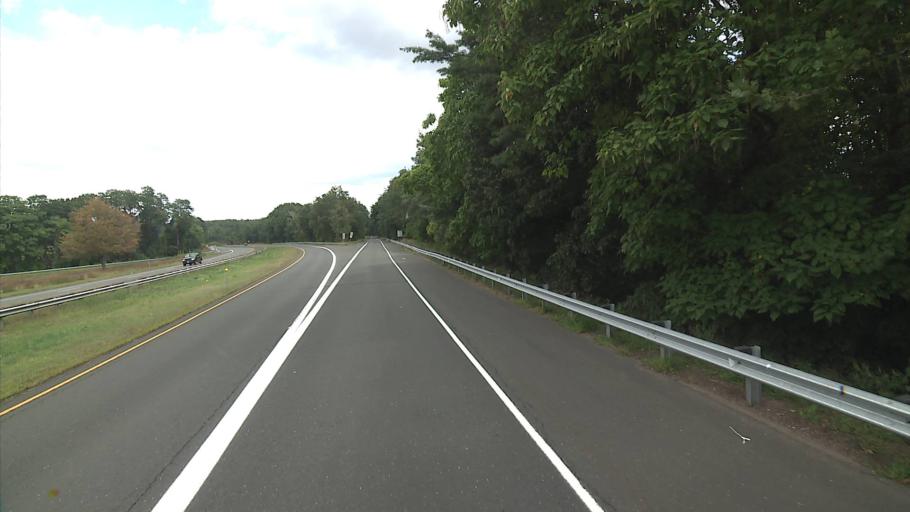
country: US
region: Connecticut
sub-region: Hartford County
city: Tariffville
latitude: 41.8892
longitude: -72.7486
